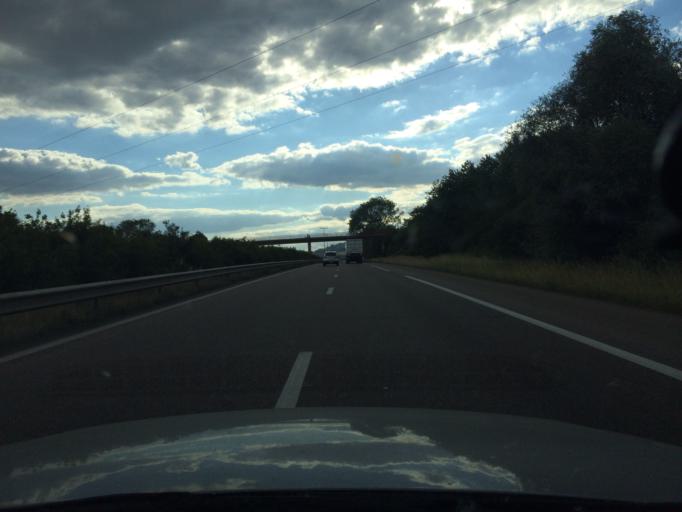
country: FR
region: Lorraine
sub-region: Departement de Meurthe-et-Moselle
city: Fleville-devant-Nancy
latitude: 48.6184
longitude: 6.2192
